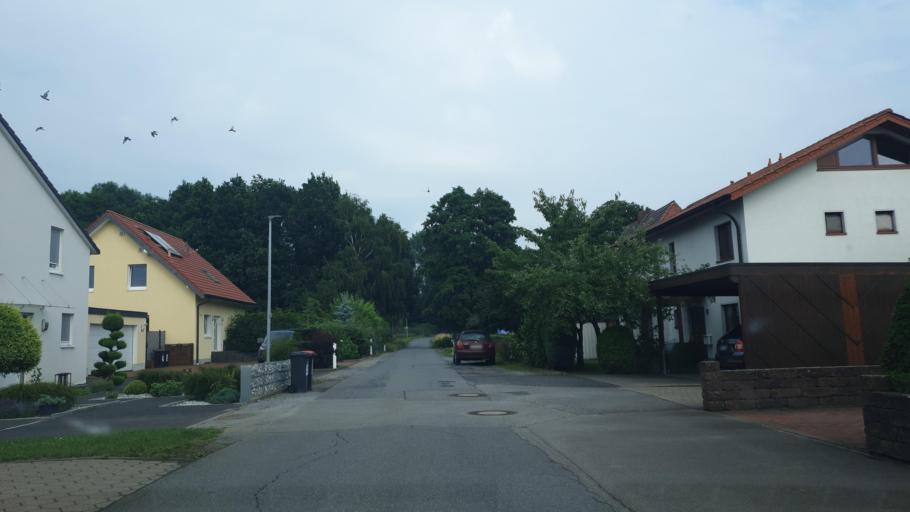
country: DE
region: North Rhine-Westphalia
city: Bad Oeynhausen
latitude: 52.2423
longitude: 8.7496
